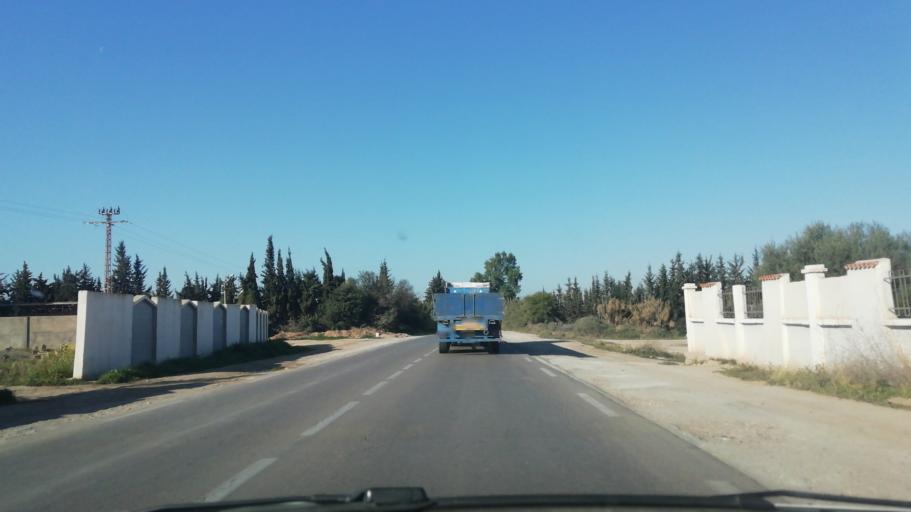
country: DZ
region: Mascara
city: Sig
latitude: 35.5765
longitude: -0.0002
